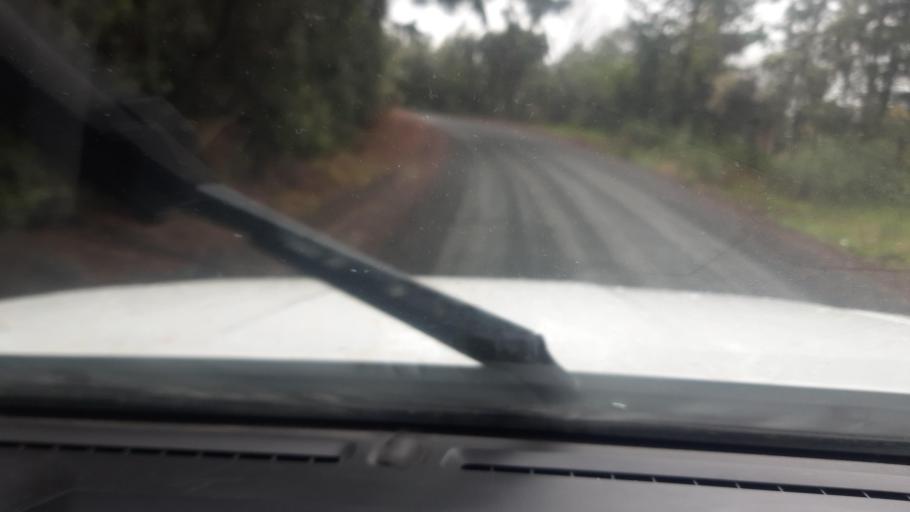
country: NZ
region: Northland
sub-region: Far North District
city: Kaitaia
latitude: -34.9860
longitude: 173.2092
